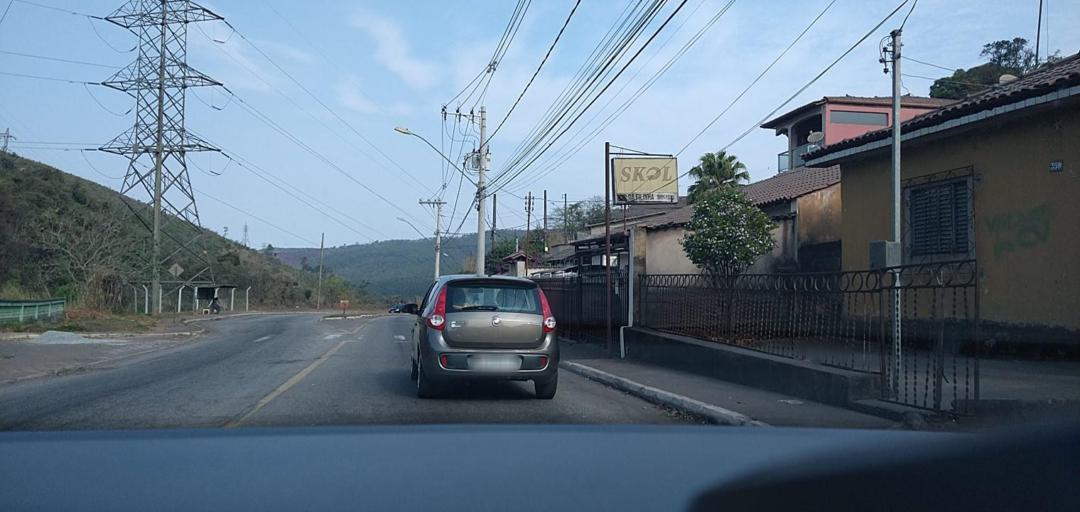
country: BR
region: Minas Gerais
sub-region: Joao Monlevade
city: Joao Monlevade
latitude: -19.8183
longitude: -43.1349
